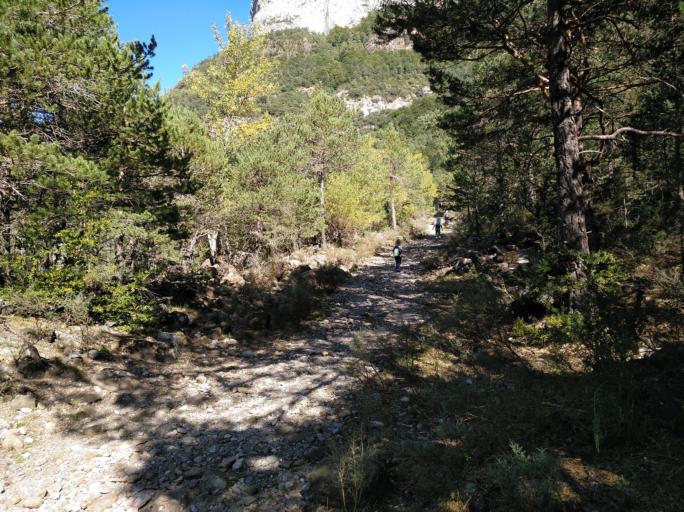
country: ES
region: Aragon
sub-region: Provincia de Huesca
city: Aragues del Puerto
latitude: 42.7958
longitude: -0.7207
